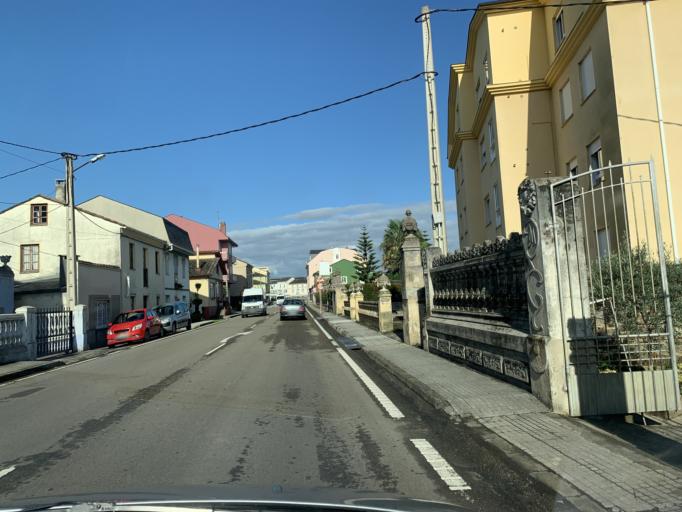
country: ES
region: Galicia
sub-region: Provincia de Lugo
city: Barreiros
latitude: 43.5437
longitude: -7.1905
